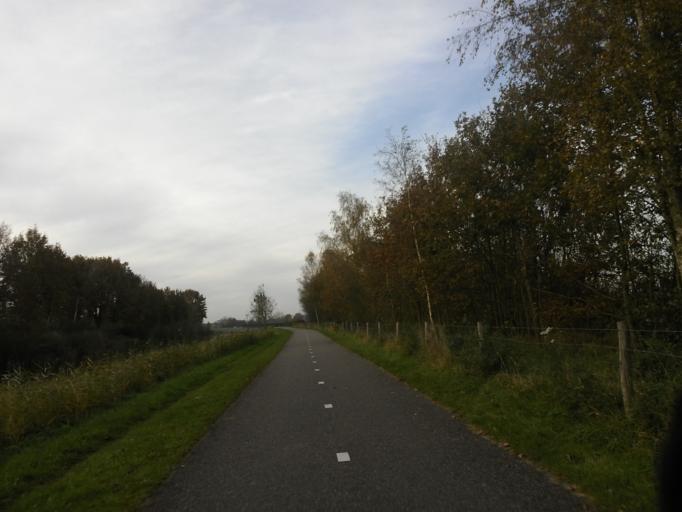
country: NL
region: Utrecht
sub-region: Gemeente Leusden
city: Leusden
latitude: 52.1444
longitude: 5.4338
